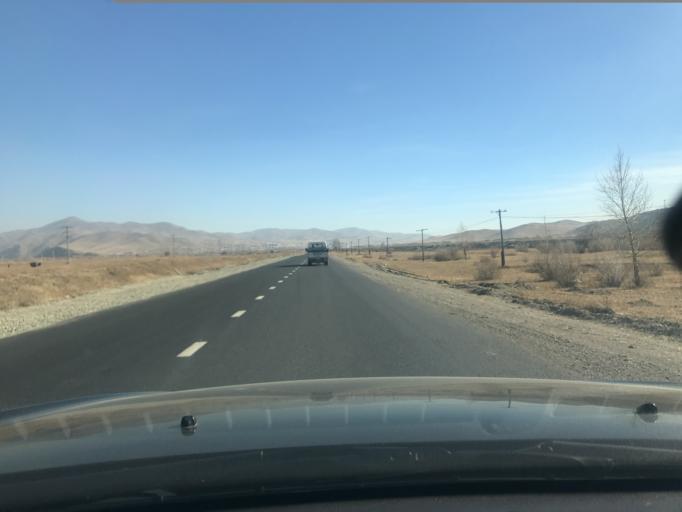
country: MN
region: Ulaanbaatar
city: Ulaanbaatar
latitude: 47.8987
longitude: 107.0410
